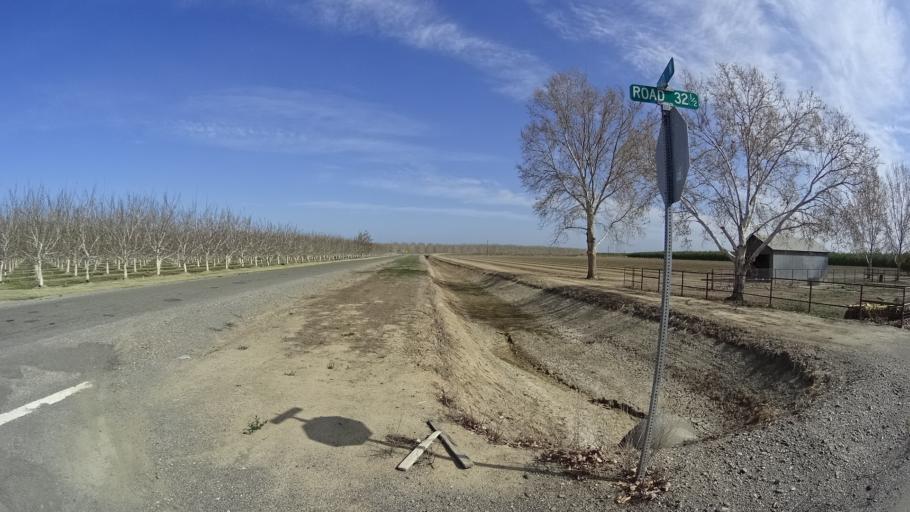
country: US
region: California
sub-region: Glenn County
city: Hamilton City
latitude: 39.6270
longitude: -122.0461
